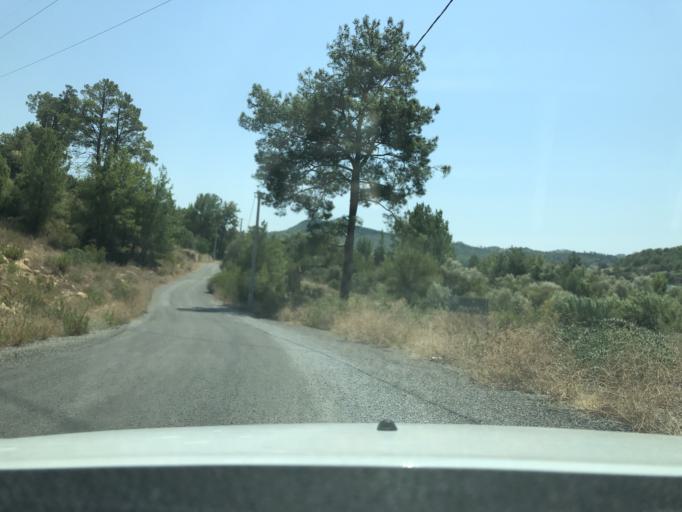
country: TR
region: Antalya
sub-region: Manavgat
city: Manavgat
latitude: 36.8766
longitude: 31.5468
